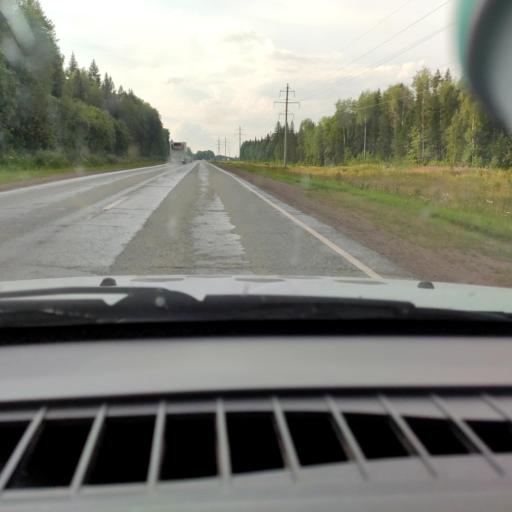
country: RU
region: Udmurtiya
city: Balezino
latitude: 57.9547
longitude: 52.9780
